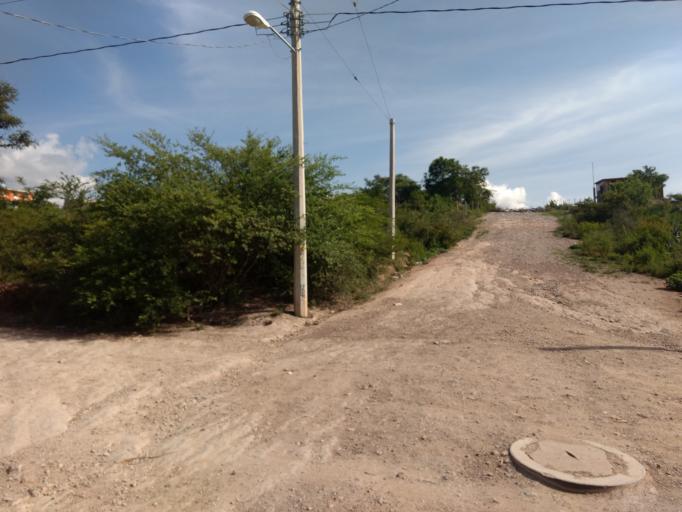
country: MX
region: Oaxaca
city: Ciudad de Huajuapam de Leon
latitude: 17.8158
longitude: -97.7981
